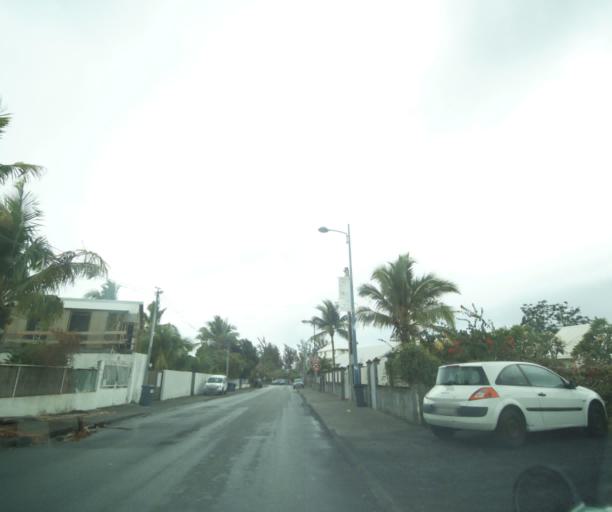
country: RE
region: Reunion
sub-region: Reunion
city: Saint-Paul
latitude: -21.0055
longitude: 55.2771
